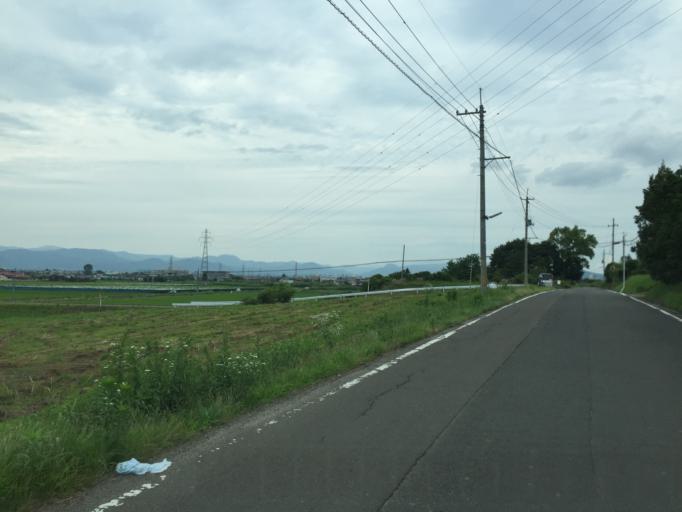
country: JP
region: Fukushima
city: Fukushima-shi
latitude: 37.7110
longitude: 140.4513
